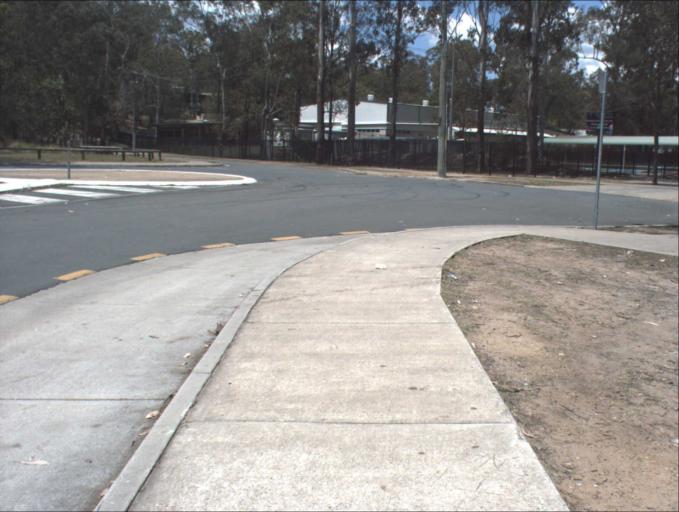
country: AU
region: Queensland
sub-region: Logan
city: Logan City
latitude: -27.6644
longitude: 153.1084
